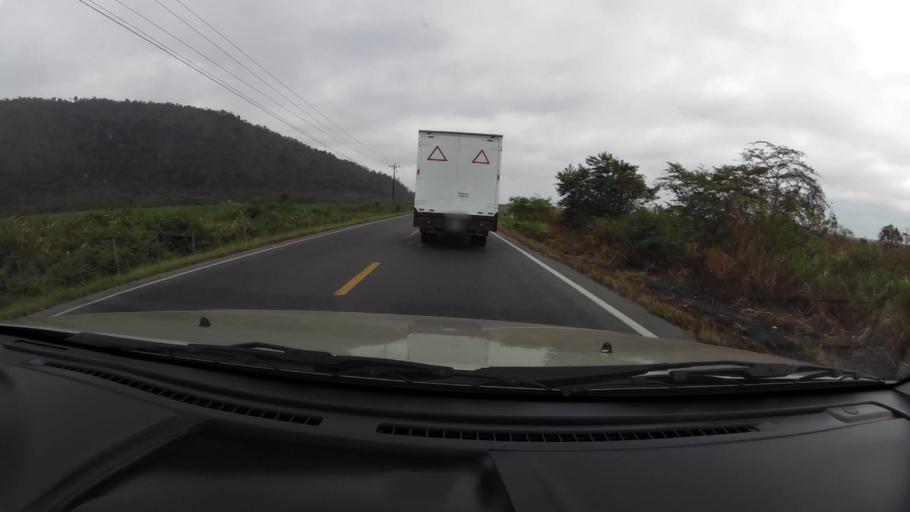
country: EC
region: Guayas
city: Naranjal
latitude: -2.4401
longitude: -79.6269
